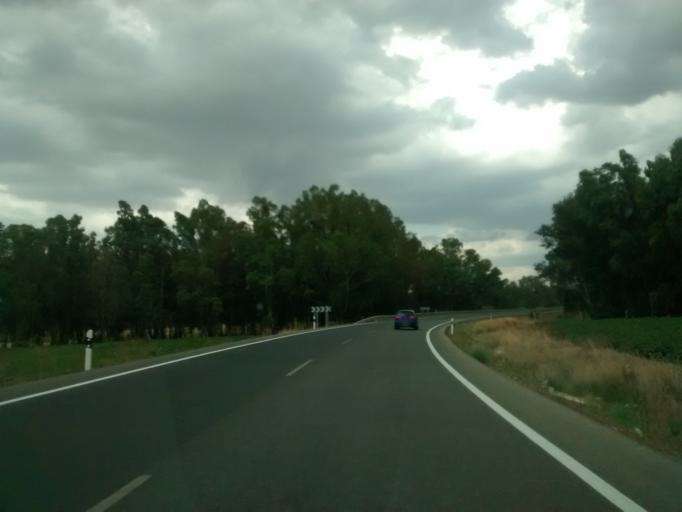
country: ES
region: Andalusia
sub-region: Provincia de Cadiz
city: Bornos
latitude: 36.8401
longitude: -5.7126
